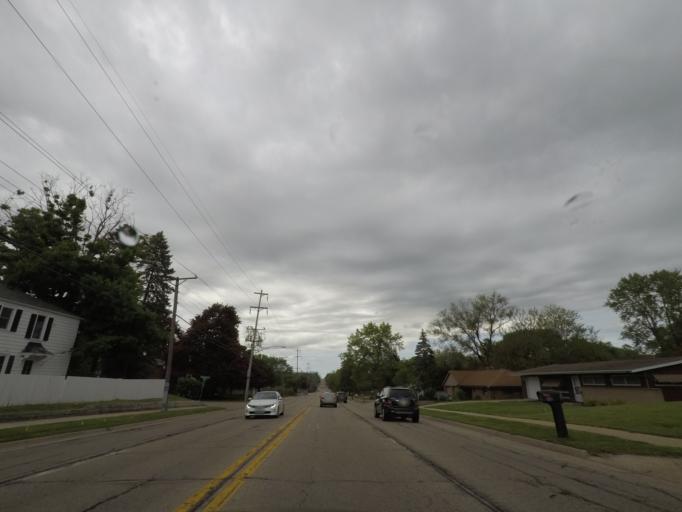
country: US
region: Illinois
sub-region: Winnebago County
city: Loves Park
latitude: 42.2897
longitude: -89.0291
